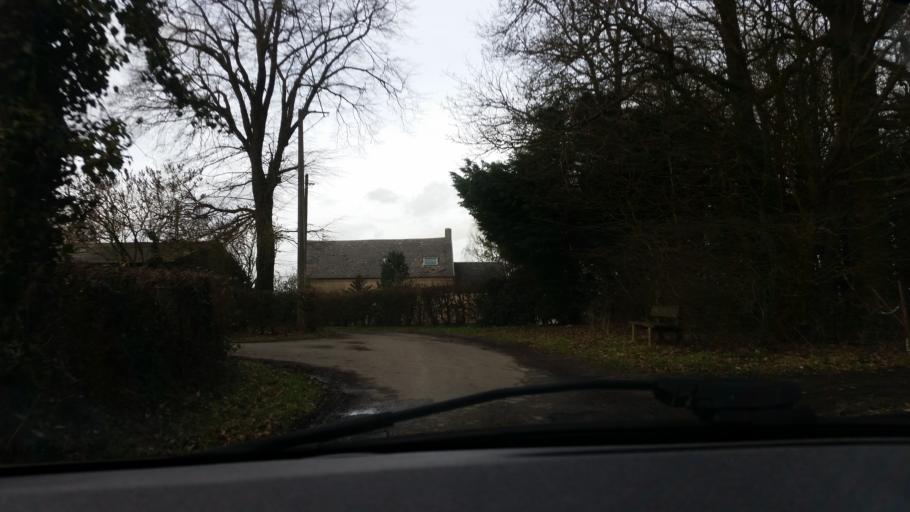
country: FR
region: Nord-Pas-de-Calais
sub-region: Departement du Nord
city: Jeumont
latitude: 50.2419
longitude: 4.1122
